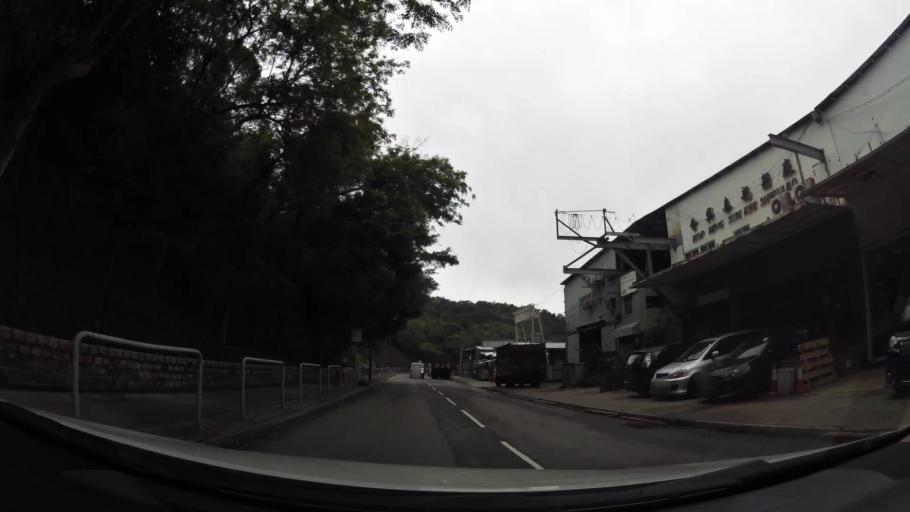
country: HK
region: Wanchai
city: Wan Chai
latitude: 22.2405
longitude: 114.1662
